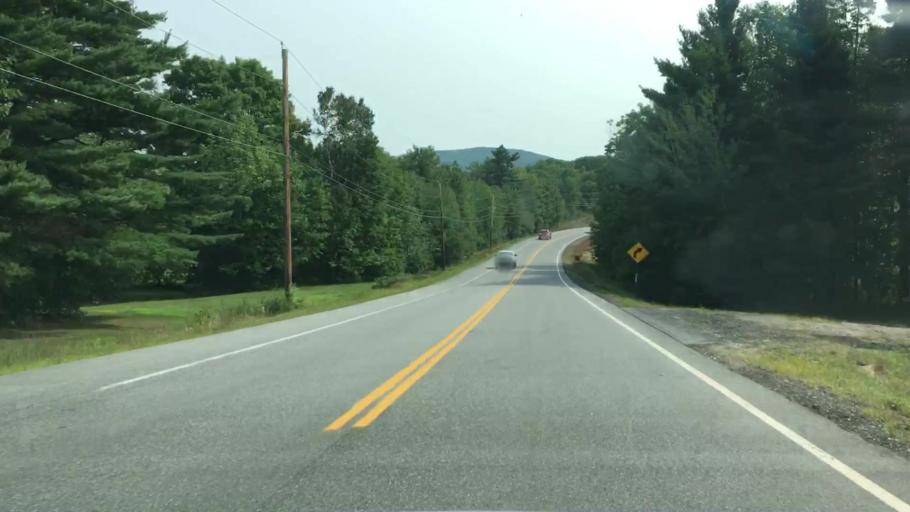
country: US
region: Maine
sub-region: Oxford County
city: Hebron
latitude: 44.2521
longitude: -70.4380
